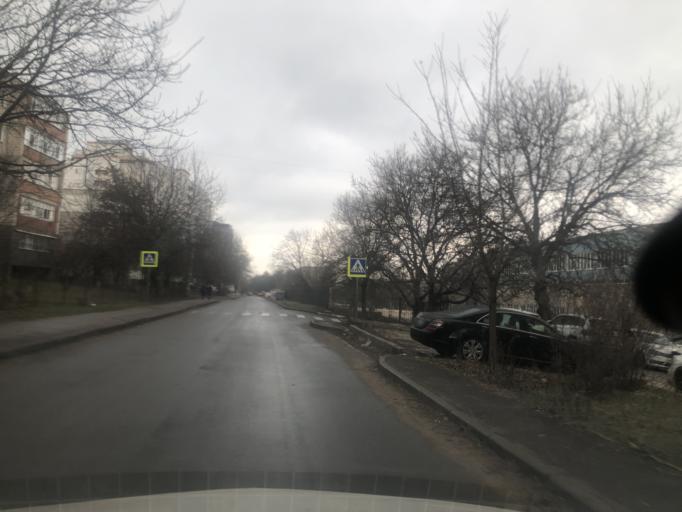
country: MD
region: Chisinau
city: Stauceni
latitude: 47.0637
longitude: 28.8431
